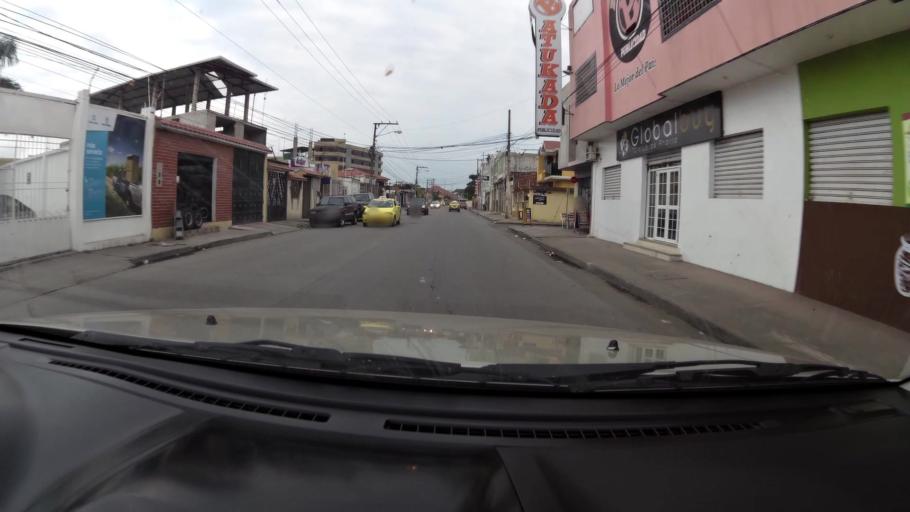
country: EC
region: El Oro
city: Machala
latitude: -3.2635
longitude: -79.9455
